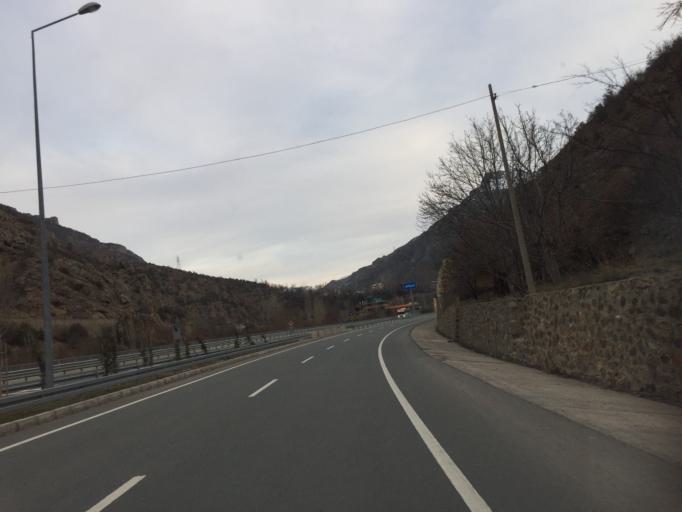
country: TR
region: Gumushane
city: Torul
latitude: 40.5461
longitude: 39.3230
